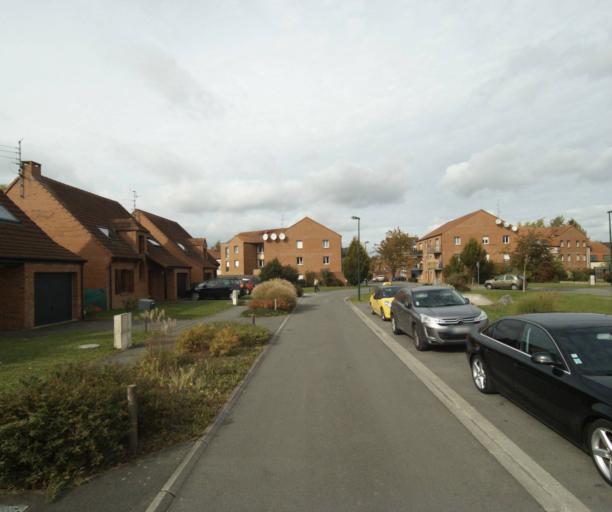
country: FR
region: Nord-Pas-de-Calais
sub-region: Departement du Nord
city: Erquinghem-Lys
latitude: 50.6757
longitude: 2.8412
